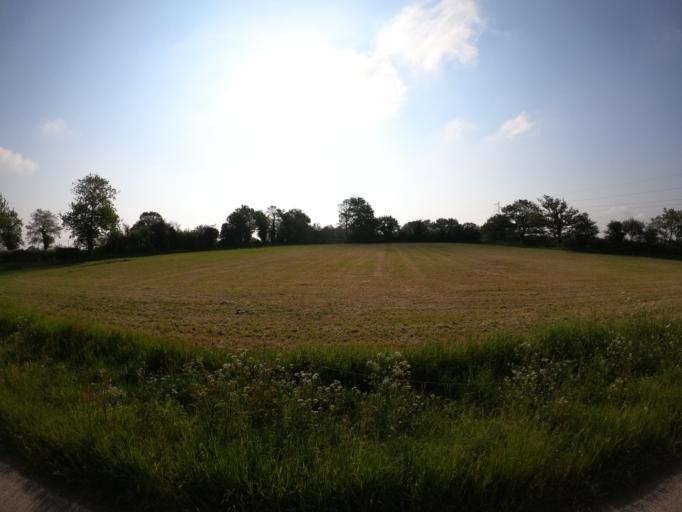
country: FR
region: Pays de la Loire
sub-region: Departement de Maine-et-Loire
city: Saint-Andre-de-la-Marche
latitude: 47.0746
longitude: -0.9951
